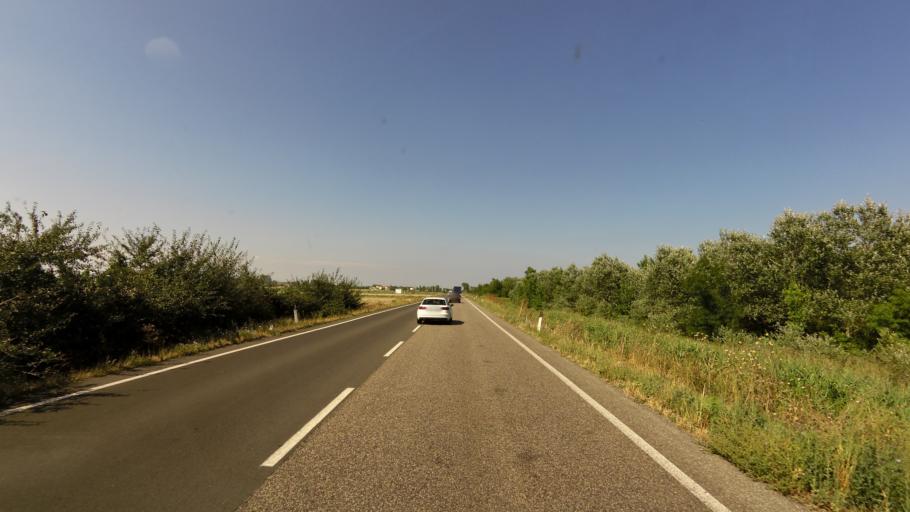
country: IT
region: Emilia-Romagna
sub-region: Provincia di Ravenna
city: Marina Romea
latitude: 44.5533
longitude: 12.2434
